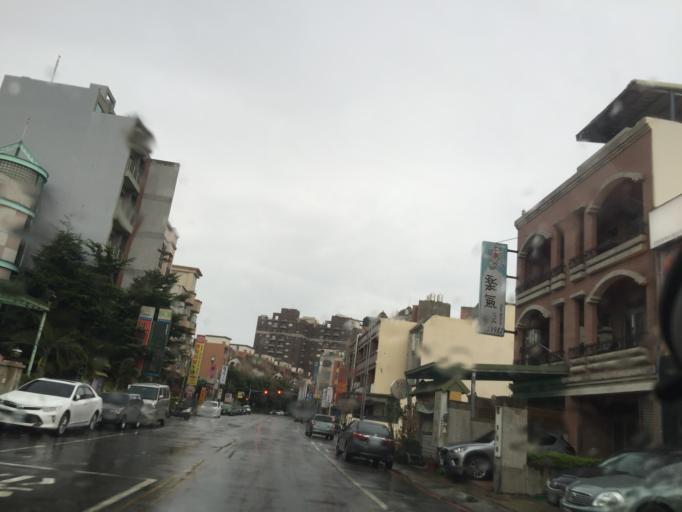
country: TW
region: Taiwan
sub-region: Hsinchu
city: Zhubei
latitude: 24.8317
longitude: 121.0154
